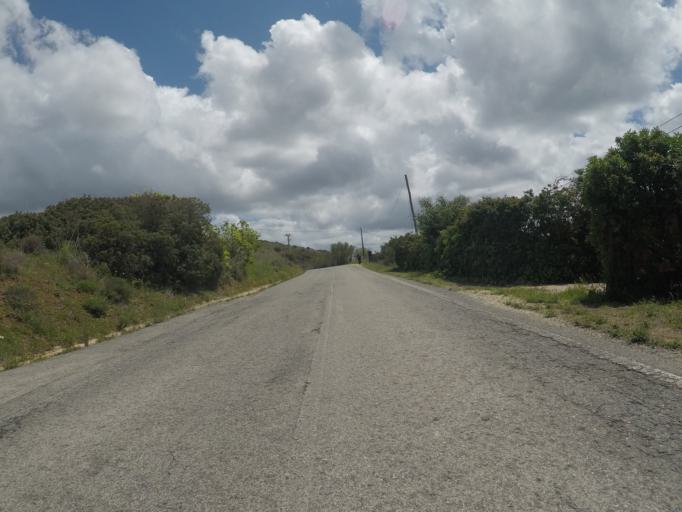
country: PT
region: Faro
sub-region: Vila do Bispo
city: Vila do Bispo
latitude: 37.0779
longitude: -8.8341
